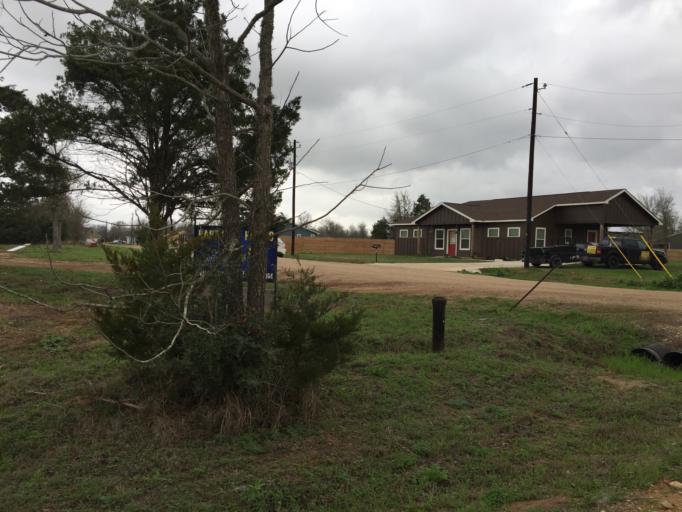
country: US
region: Texas
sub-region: Bastrop County
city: Bastrop
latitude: 30.0861
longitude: -97.3198
